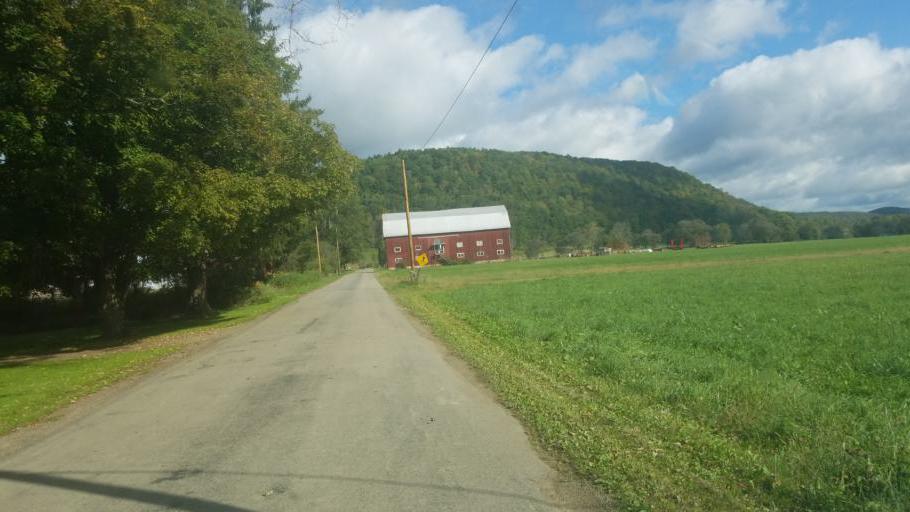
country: US
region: New York
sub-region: Cattaraugus County
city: Weston Mills
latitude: 42.1325
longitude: -78.3442
